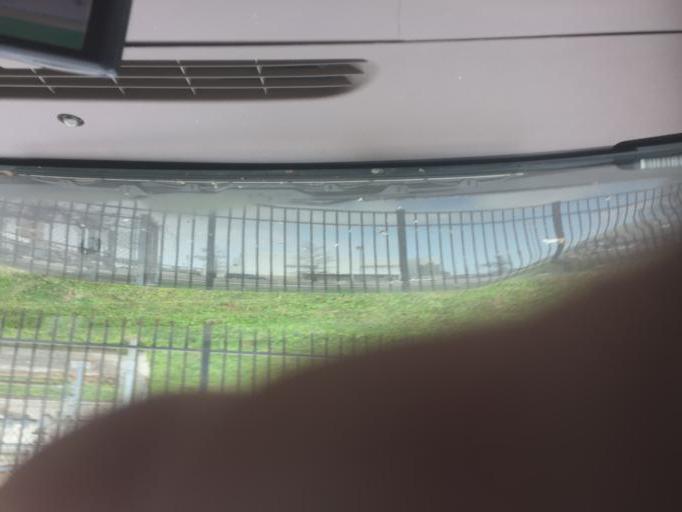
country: US
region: Louisiana
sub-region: Saint Bernard Parish
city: Arabi
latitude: 29.9987
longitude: -90.0318
